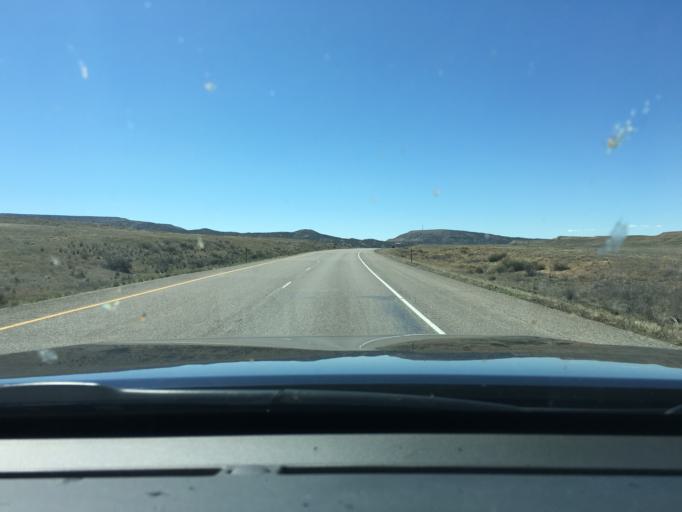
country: US
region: Colorado
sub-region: Mesa County
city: Loma
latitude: 39.2306
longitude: -108.9167
